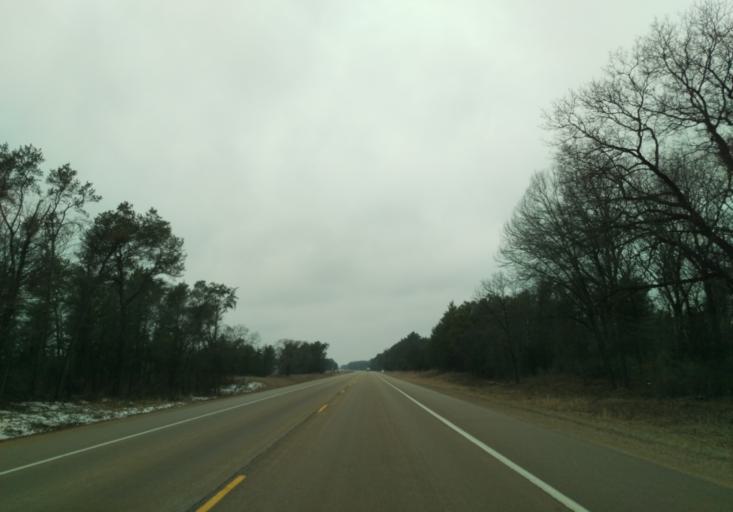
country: US
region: Wisconsin
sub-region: Sauk County
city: Spring Green
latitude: 43.1905
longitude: -90.1520
